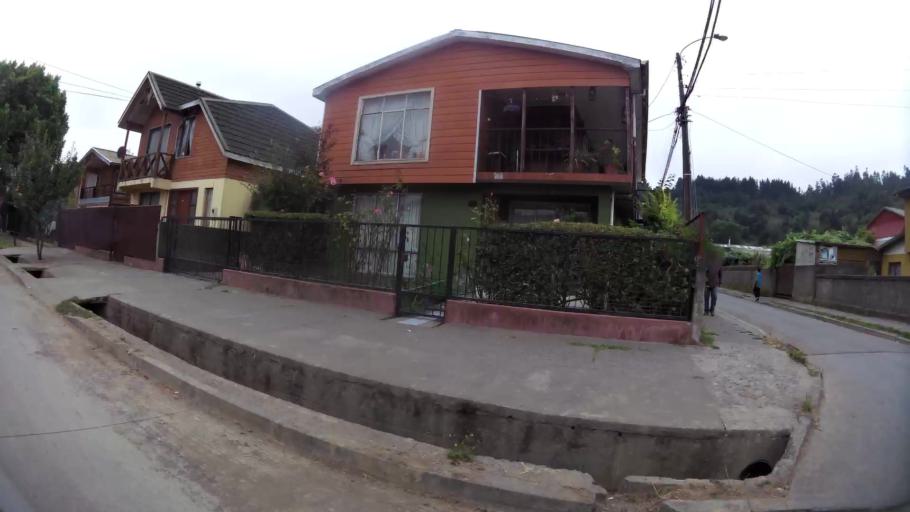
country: CL
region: Biobio
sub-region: Provincia de Concepcion
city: Concepcion
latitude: -36.8337
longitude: -73.0009
